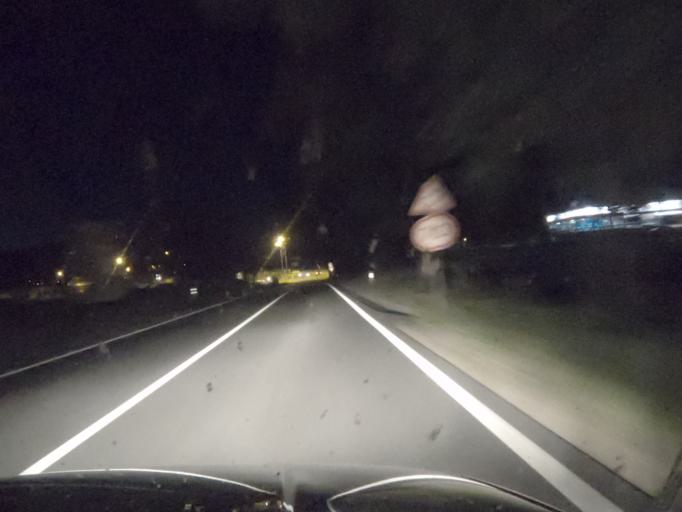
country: PT
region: Guarda
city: Alcains
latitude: 39.9853
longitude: -7.4582
